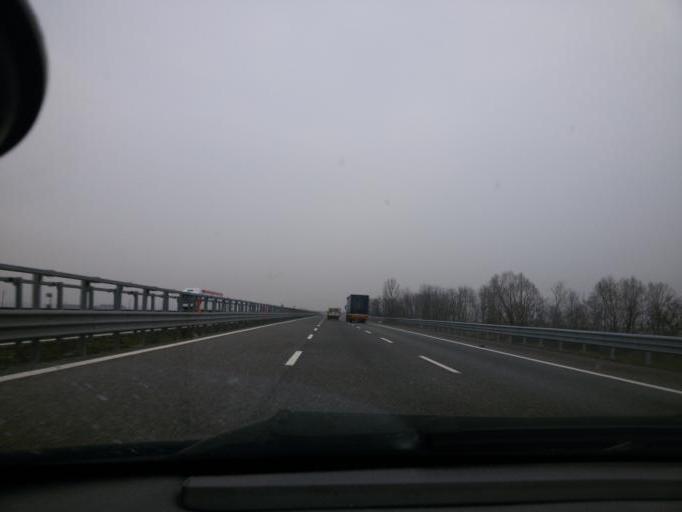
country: IT
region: Piedmont
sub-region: Provincia di Vercelli
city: Caresana
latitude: 45.2170
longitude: 8.4812
